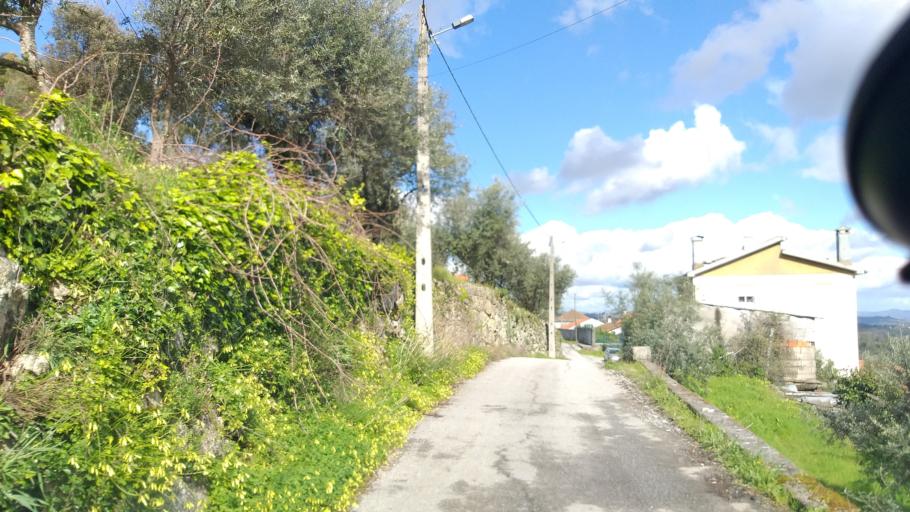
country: PT
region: Guarda
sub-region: Fornos de Algodres
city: Fornos de Algodres
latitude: 40.6186
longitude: -7.5436
